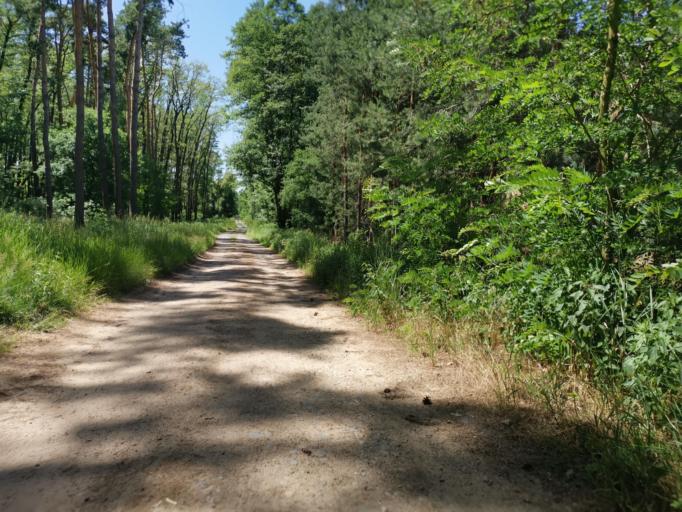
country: CZ
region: South Moravian
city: Bzenec
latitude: 48.9655
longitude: 17.2777
